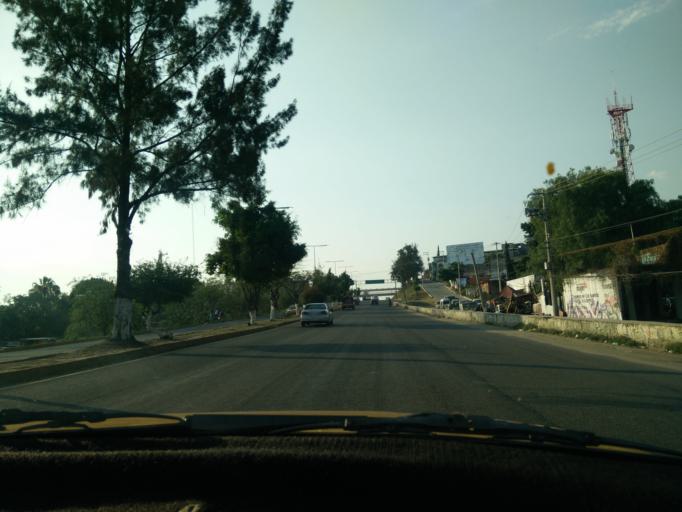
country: MX
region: Oaxaca
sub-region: Santa Maria Atzompa
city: San Jeronimo Yahuiche
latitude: 17.0946
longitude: -96.7487
